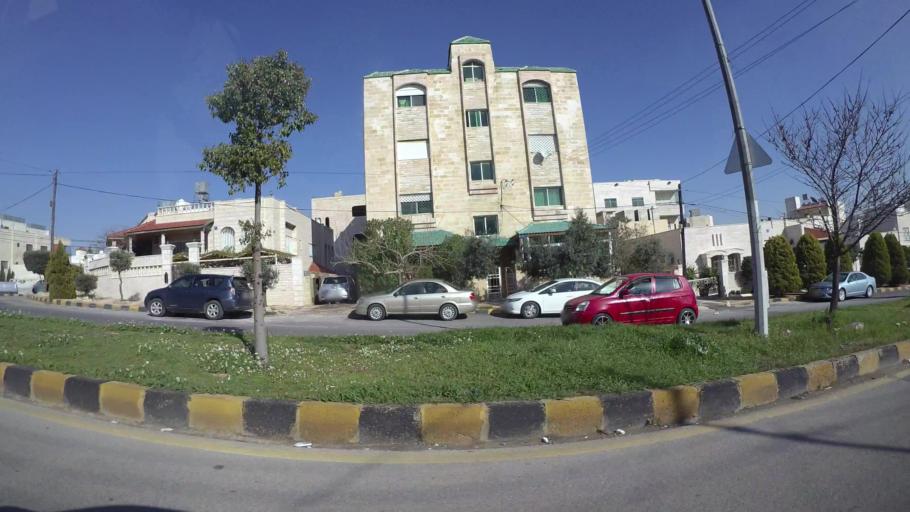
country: JO
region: Amman
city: Amman
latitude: 31.9729
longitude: 35.9384
